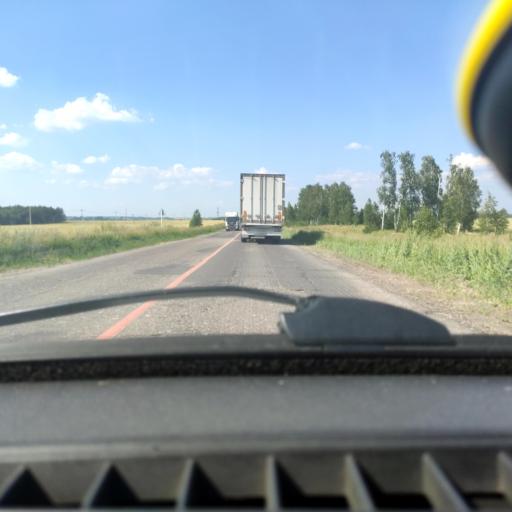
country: RU
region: Samara
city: Povolzhskiy
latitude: 53.7259
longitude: 49.7517
